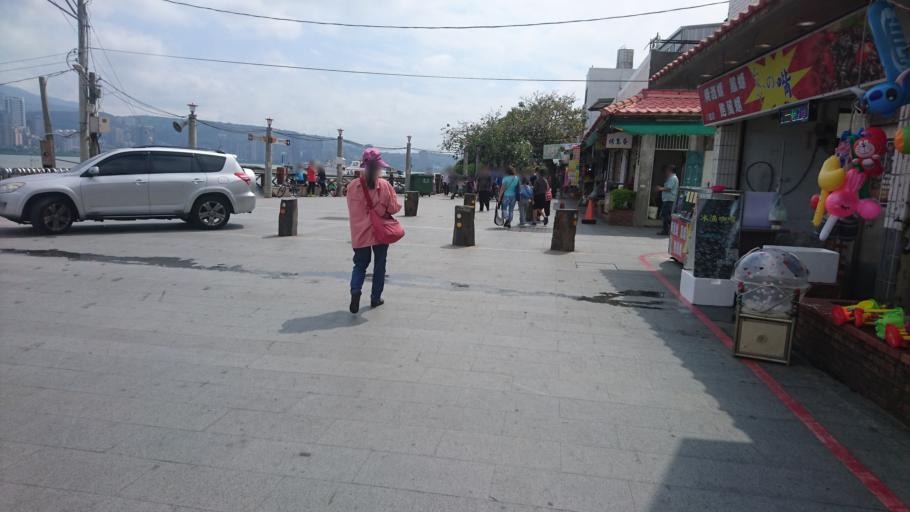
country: TW
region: Taipei
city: Taipei
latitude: 25.1596
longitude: 121.4341
